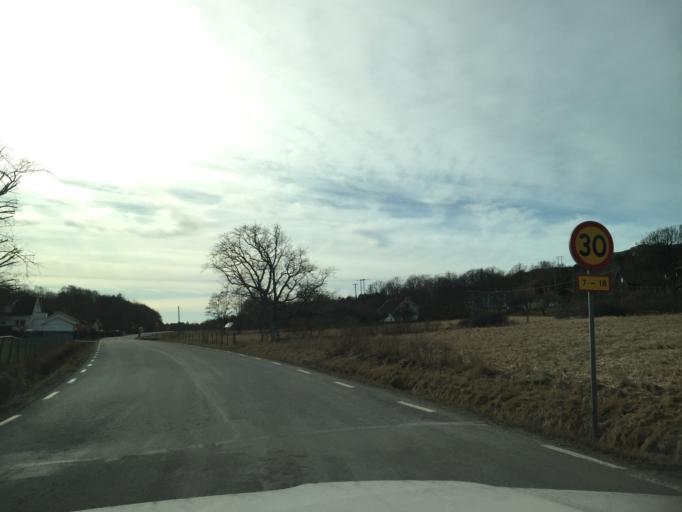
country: SE
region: Vaestra Goetaland
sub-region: Tjorns Kommun
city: Skaerhamn
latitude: 58.0350
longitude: 11.5511
